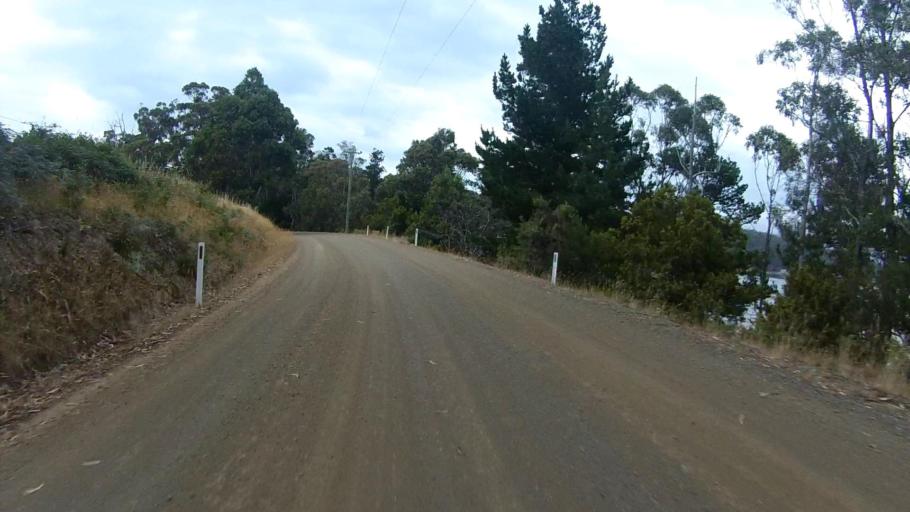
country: AU
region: Tasmania
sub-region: Huon Valley
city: Cygnet
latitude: -43.2360
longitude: 147.0988
